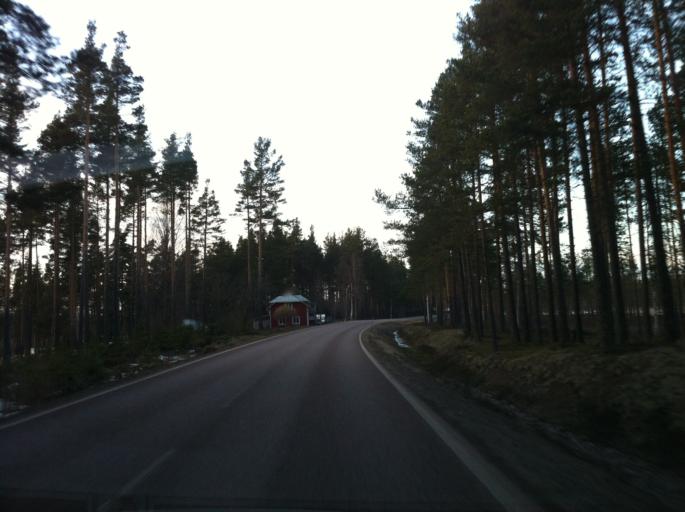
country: SE
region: Dalarna
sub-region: Vansbro Kommun
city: Vansbro
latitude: 60.5382
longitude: 14.2081
